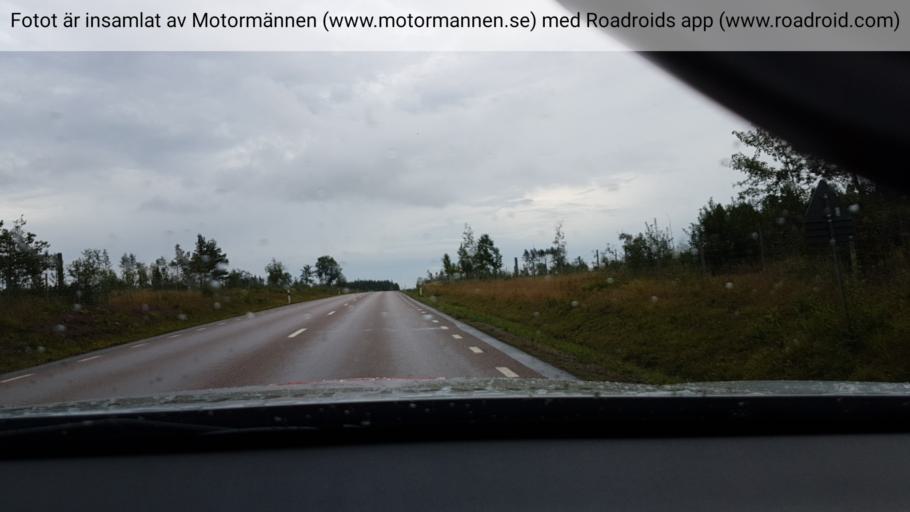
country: SE
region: Uppsala
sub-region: Tierps Kommun
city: Karlholmsbruk
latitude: 60.4370
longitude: 17.7921
